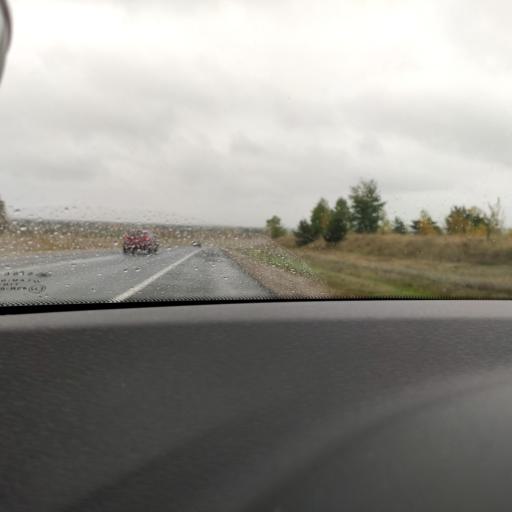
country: RU
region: Samara
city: Mirnyy
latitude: 53.6364
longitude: 50.2361
